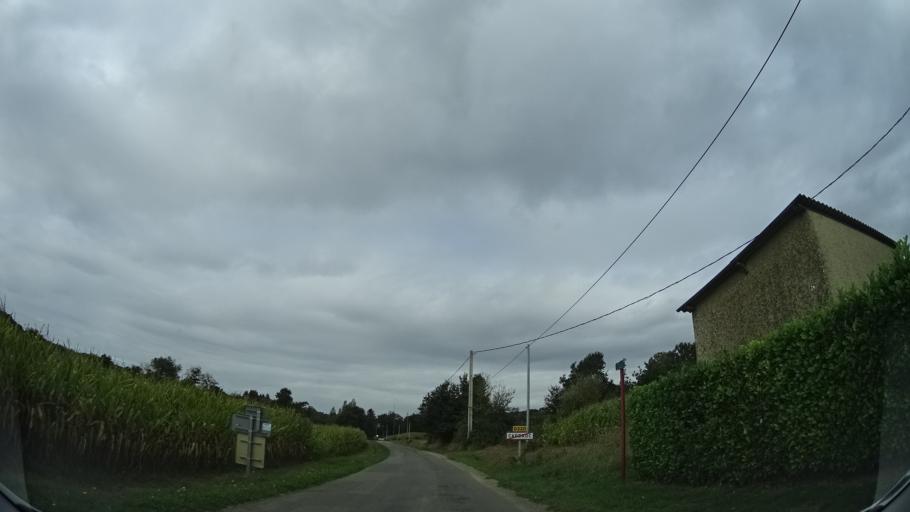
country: FR
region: Brittany
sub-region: Departement d'Ille-et-Vilaine
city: Irodouer
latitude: 48.2845
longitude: -1.8935
